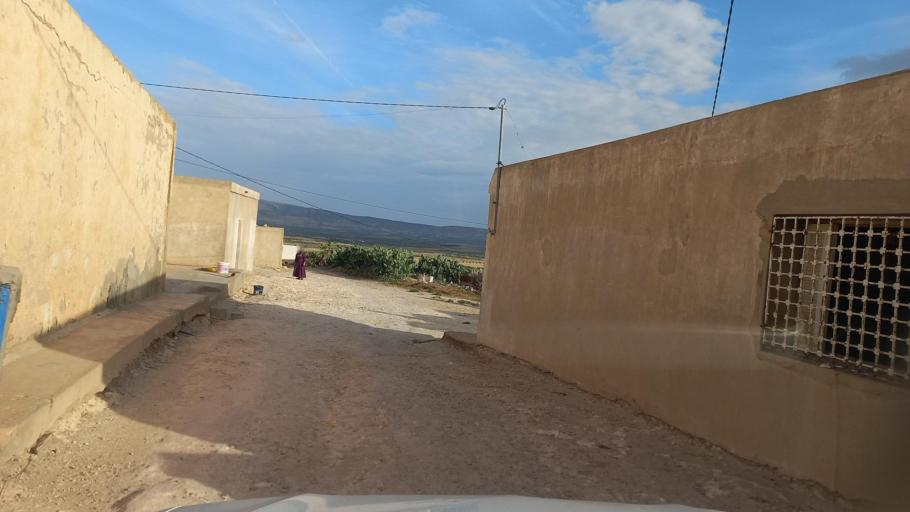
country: TN
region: Al Qasrayn
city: Sbiba
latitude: 35.4536
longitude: 9.0870
